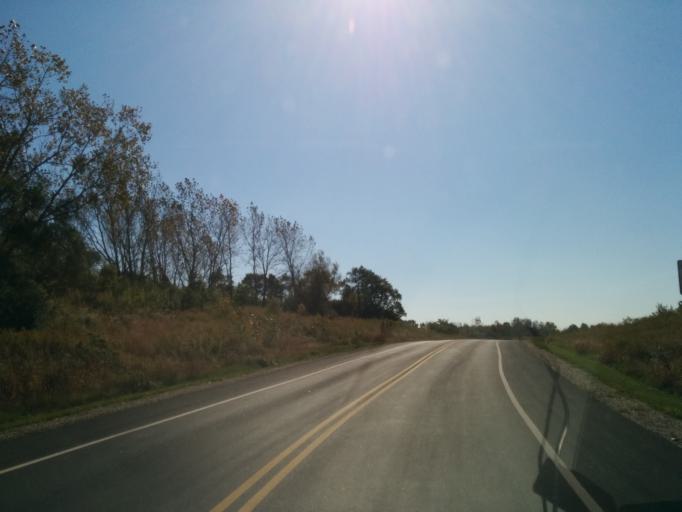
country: US
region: Illinois
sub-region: DuPage County
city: Hanover Park
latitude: 41.9603
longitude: -88.1278
